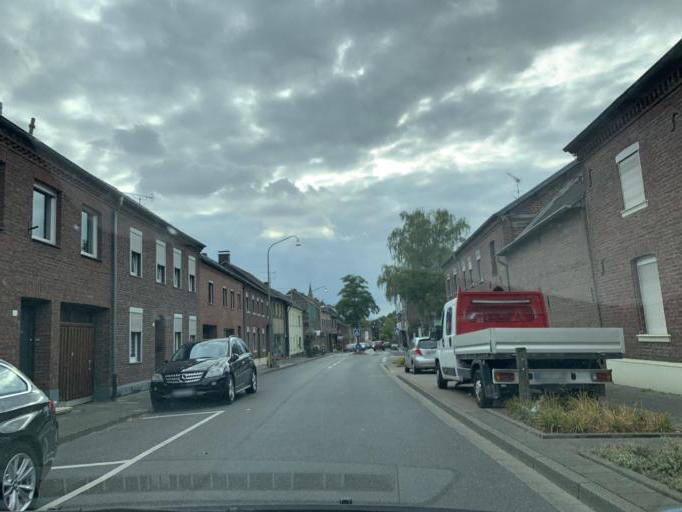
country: DE
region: North Rhine-Westphalia
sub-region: Regierungsbezirk Koln
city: Wassenberg
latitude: 51.0976
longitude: 6.1913
